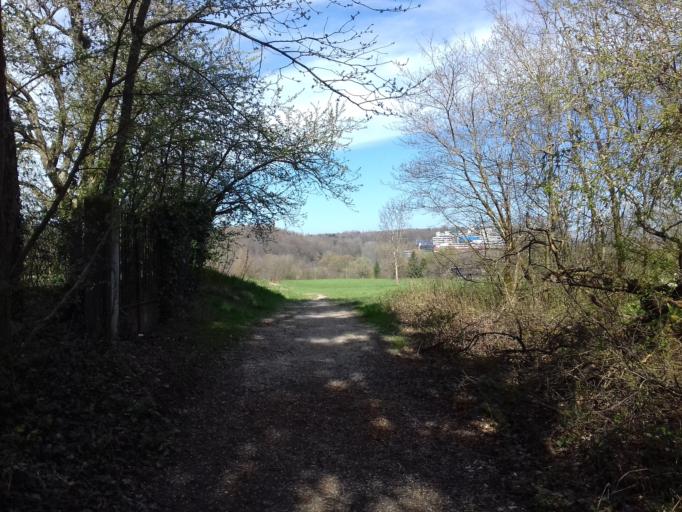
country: DE
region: Baden-Wuerttemberg
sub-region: Freiburg Region
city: Konstanz
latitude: 47.6815
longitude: 9.1963
